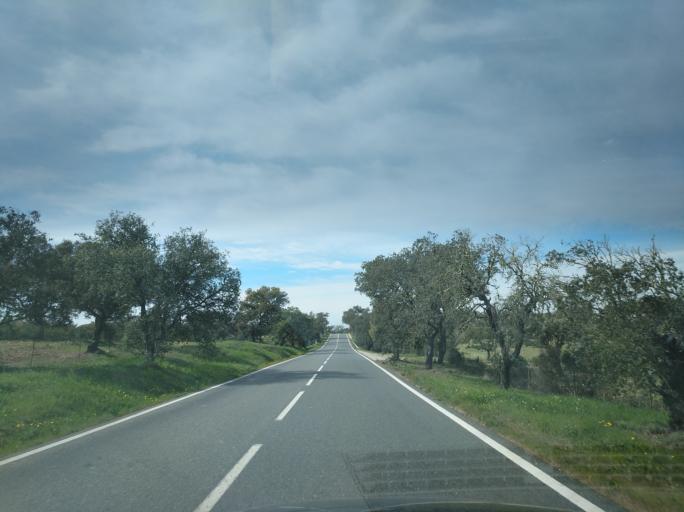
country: PT
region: Beja
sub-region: Mertola
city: Mertola
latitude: 37.7405
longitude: -7.7852
